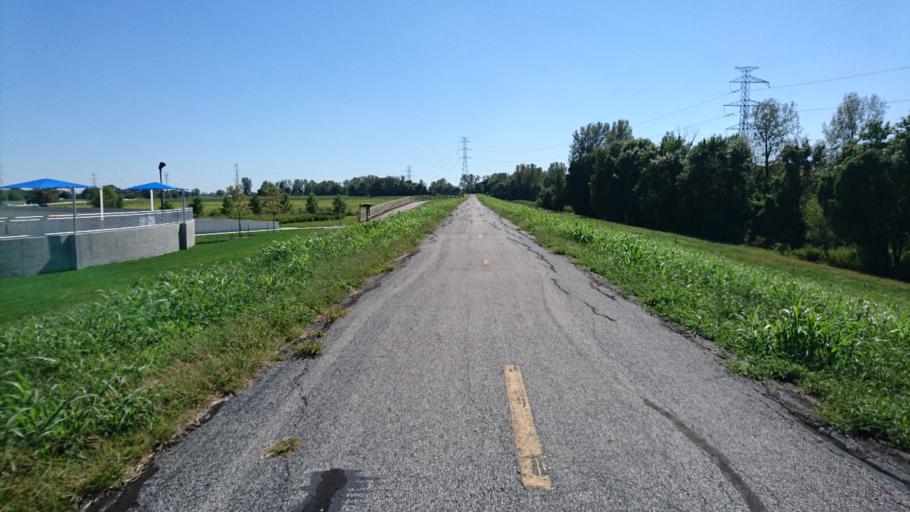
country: US
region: Illinois
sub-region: Madison County
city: Hartford
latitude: 38.8114
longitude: -90.1012
